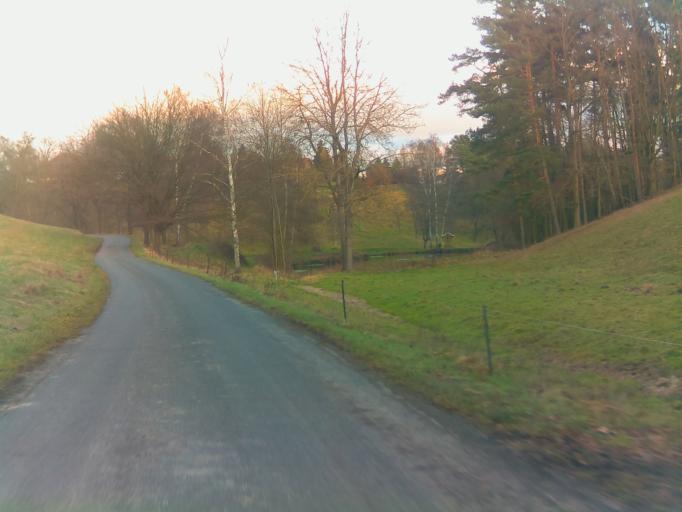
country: DE
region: Thuringia
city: Rudolstadt
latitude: 50.7586
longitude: 11.3478
